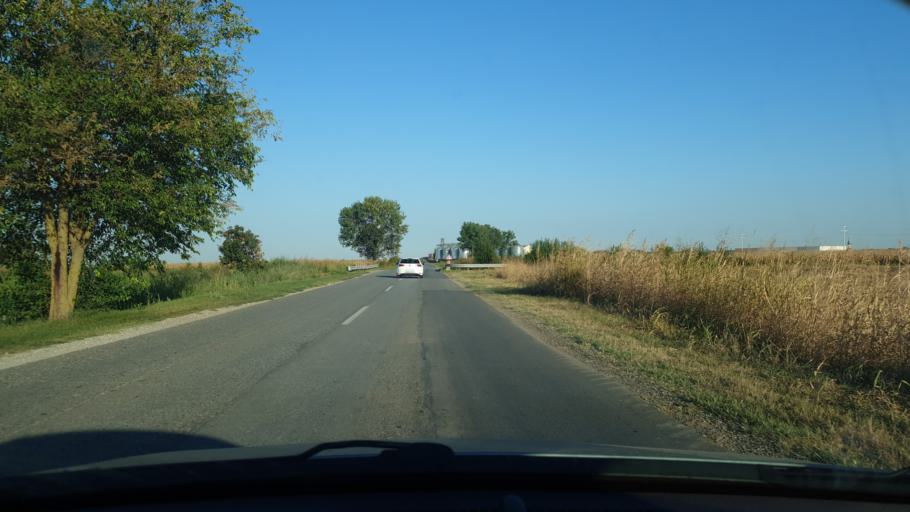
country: RS
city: Putinci
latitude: 44.9661
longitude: 19.9116
